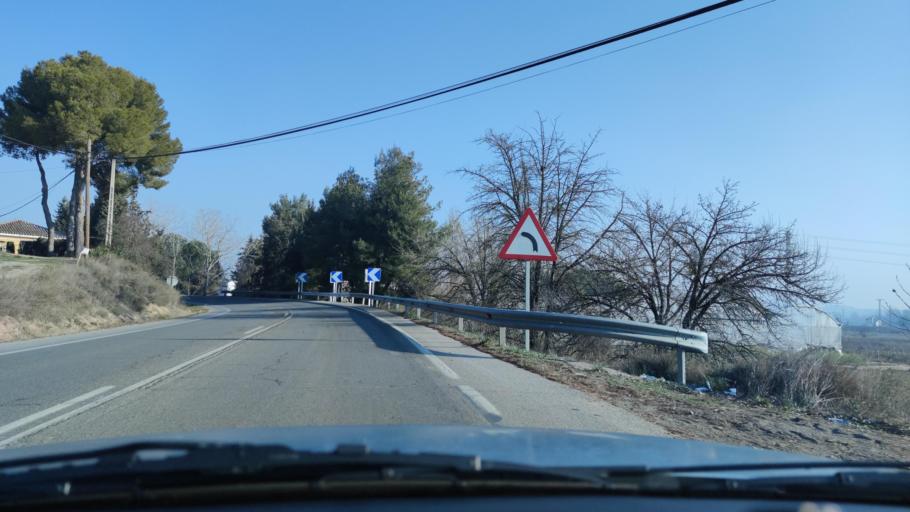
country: ES
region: Catalonia
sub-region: Provincia de Lleida
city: Lleida
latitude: 41.6322
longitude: 0.6353
